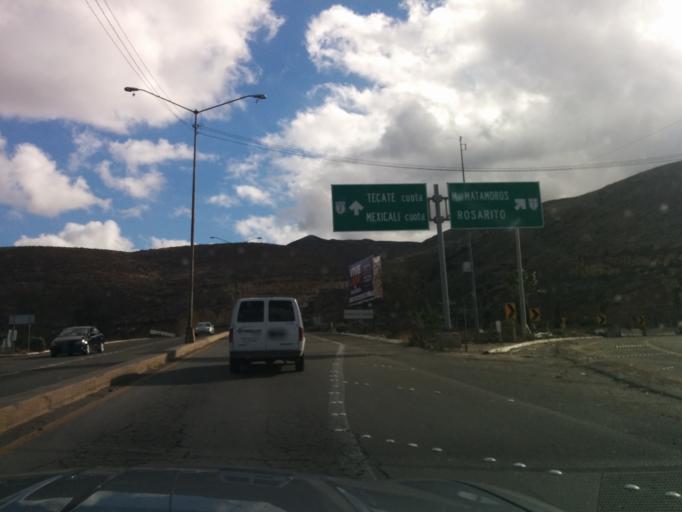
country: MX
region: Baja California
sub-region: Tijuana
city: Ejido Javier Rojo Gomez
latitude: 32.5423
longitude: -116.8560
